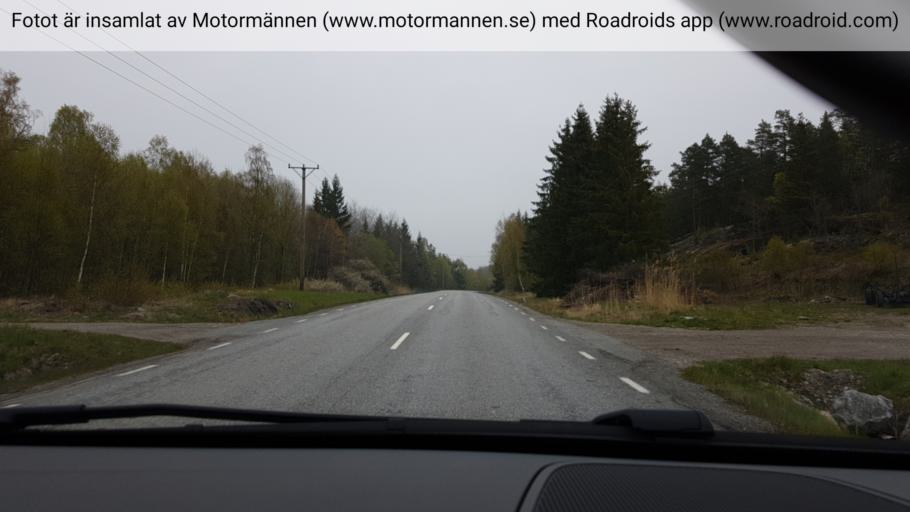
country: SE
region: Stockholm
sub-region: Nynashamns Kommun
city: Nynashamn
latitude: 58.9603
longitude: 17.9784
